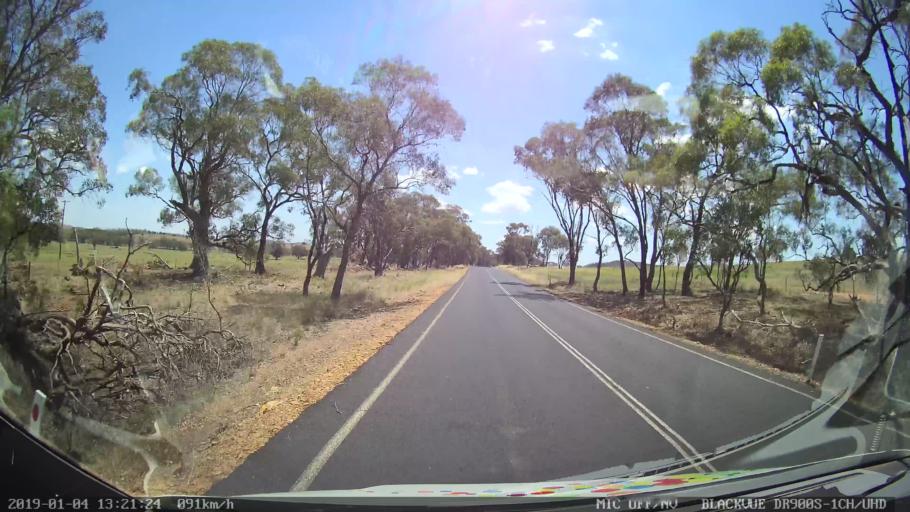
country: AU
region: New South Wales
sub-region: Parkes
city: Peak Hill
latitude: -32.7372
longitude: 148.5777
